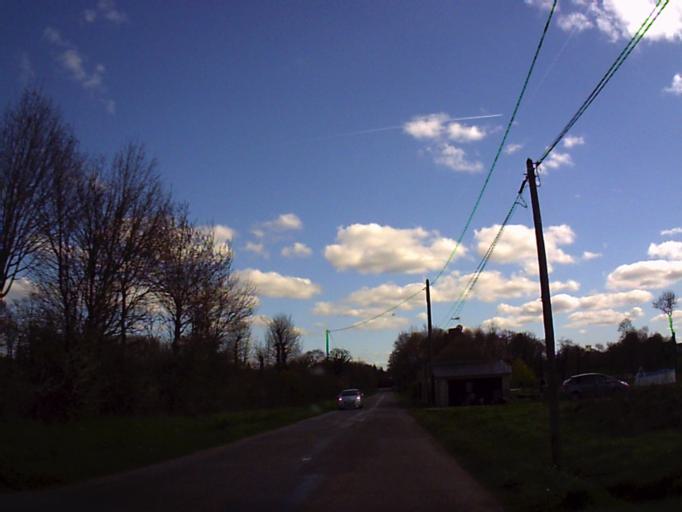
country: FR
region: Brittany
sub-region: Departement d'Ille-et-Vilaine
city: Gael
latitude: 48.1319
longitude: -2.1576
